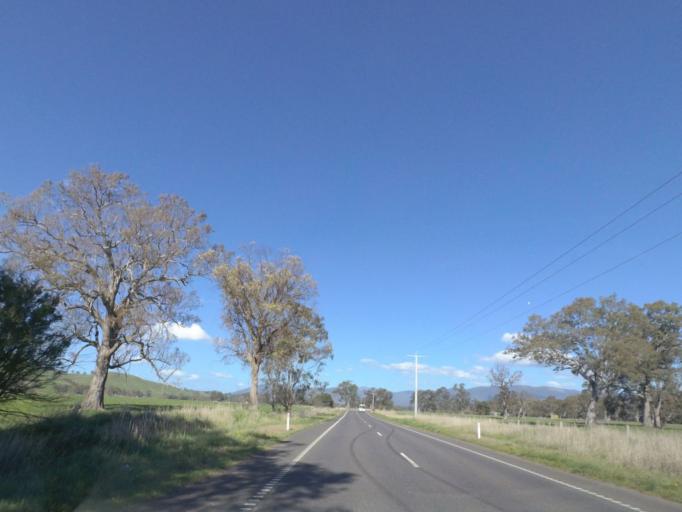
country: AU
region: Victoria
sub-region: Murrindindi
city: Alexandra
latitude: -37.2234
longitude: 145.7397
